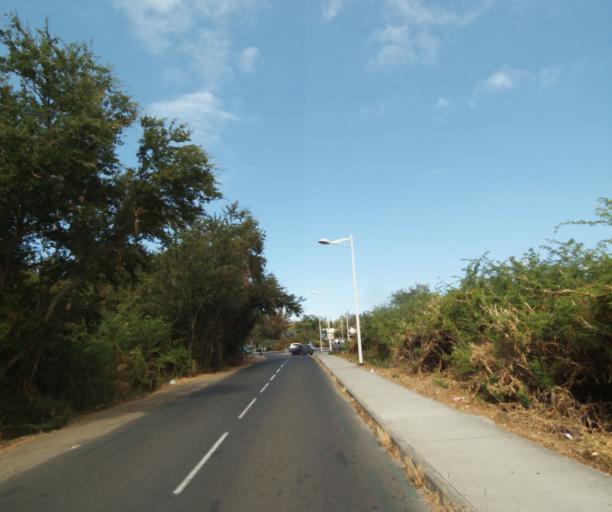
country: RE
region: Reunion
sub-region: Reunion
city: Trois-Bassins
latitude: -21.0845
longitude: 55.2329
